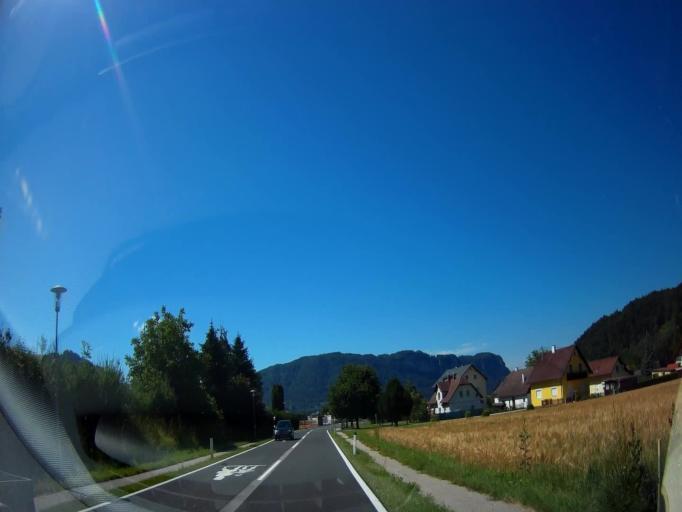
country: AT
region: Carinthia
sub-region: Politischer Bezirk Volkermarkt
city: Gallizien
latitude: 46.5518
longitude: 14.5128
